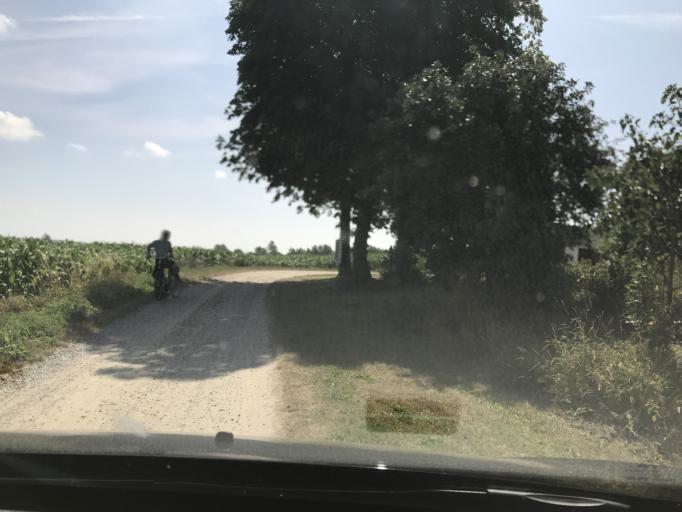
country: DK
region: South Denmark
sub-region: AEro Kommune
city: AEroskobing
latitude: 54.9066
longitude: 10.3215
